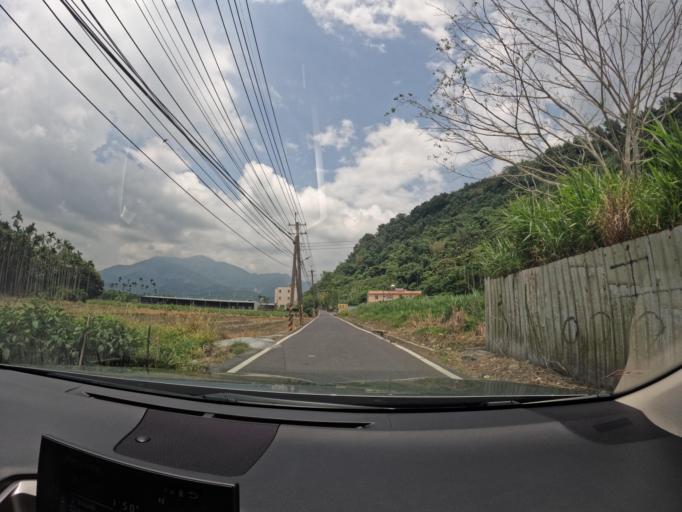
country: TW
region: Taiwan
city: Lugu
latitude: 23.8062
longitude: 120.7962
